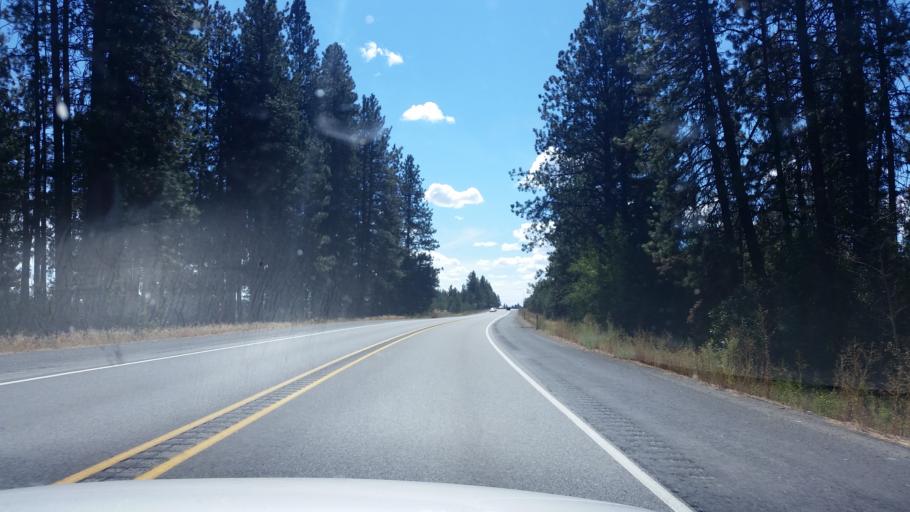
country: US
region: Washington
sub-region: Spokane County
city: Cheney
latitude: 47.5178
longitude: -117.5647
